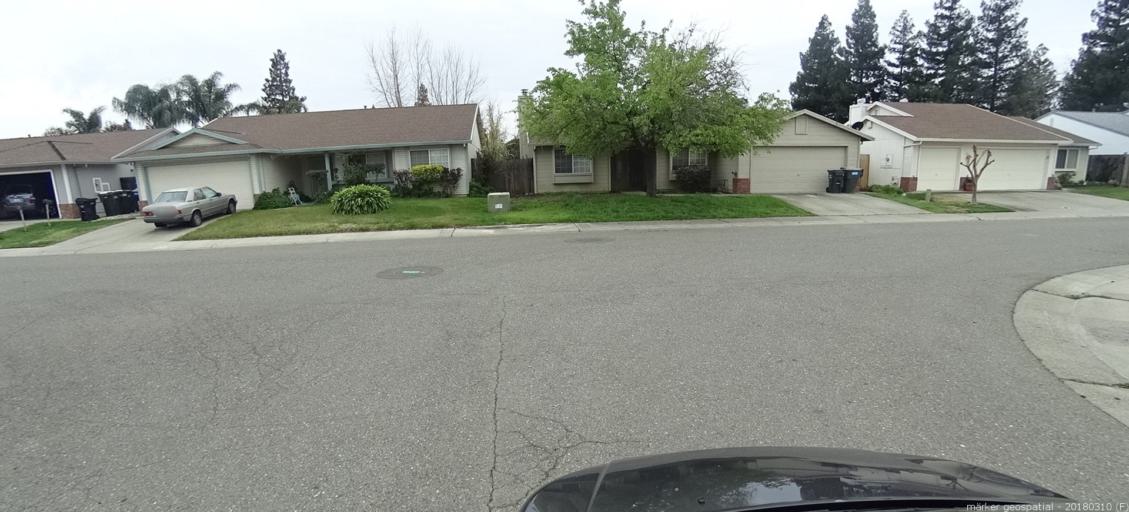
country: US
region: California
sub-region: Sacramento County
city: Florin
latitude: 38.4784
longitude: -121.3819
